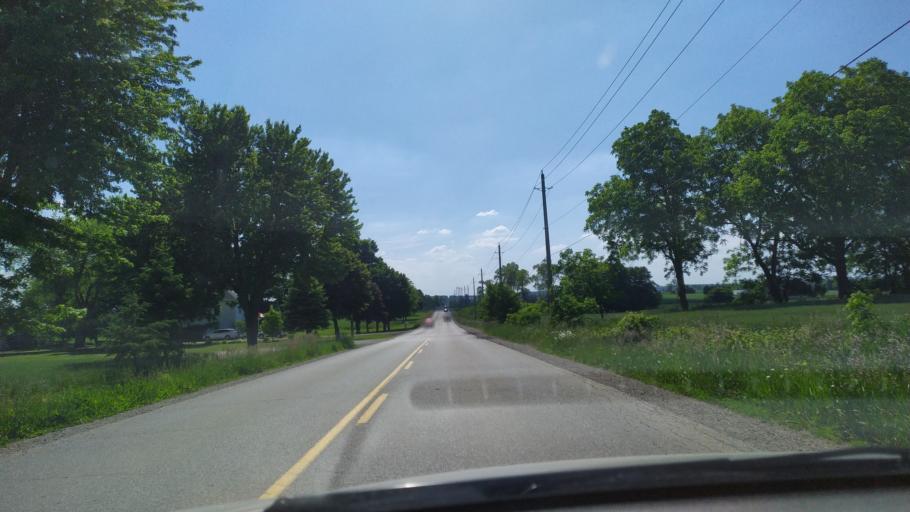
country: CA
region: Ontario
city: Kitchener
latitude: 43.3762
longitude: -80.5246
